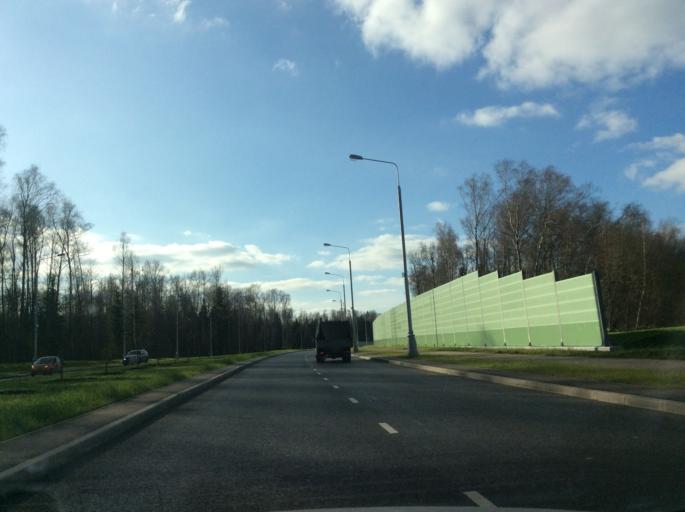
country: RU
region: Moskovskaya
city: Vatutinki
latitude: 55.4868
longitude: 37.3886
